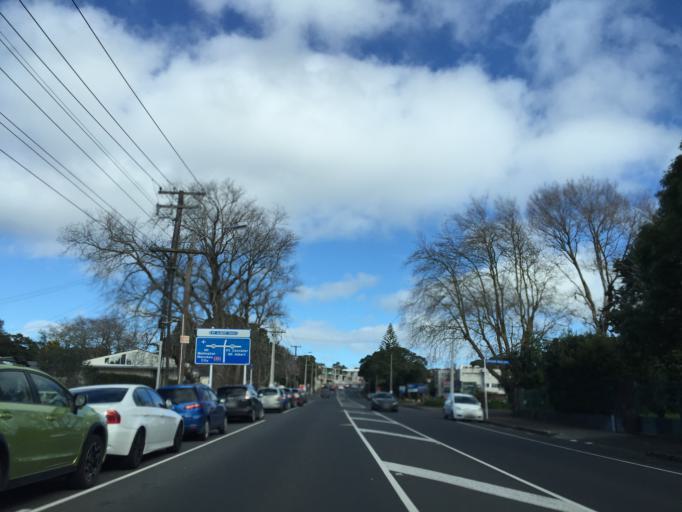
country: NZ
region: Auckland
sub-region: Auckland
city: Auckland
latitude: -36.9068
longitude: 174.7589
